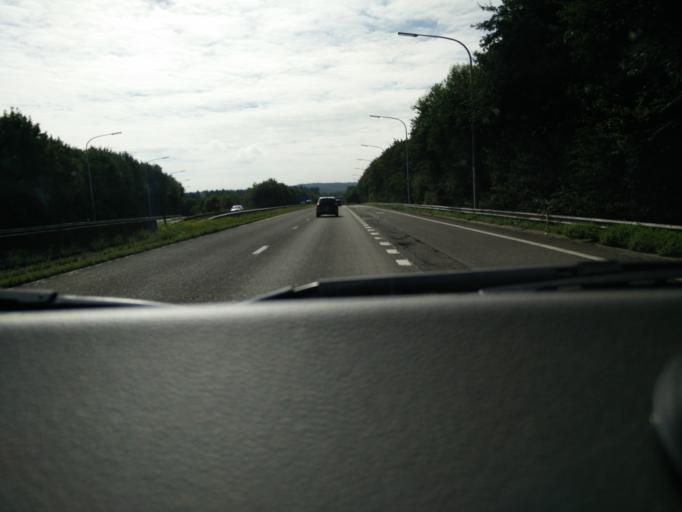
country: BE
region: Wallonia
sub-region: Province de Namur
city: Houyet
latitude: 50.2246
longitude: 5.0579
